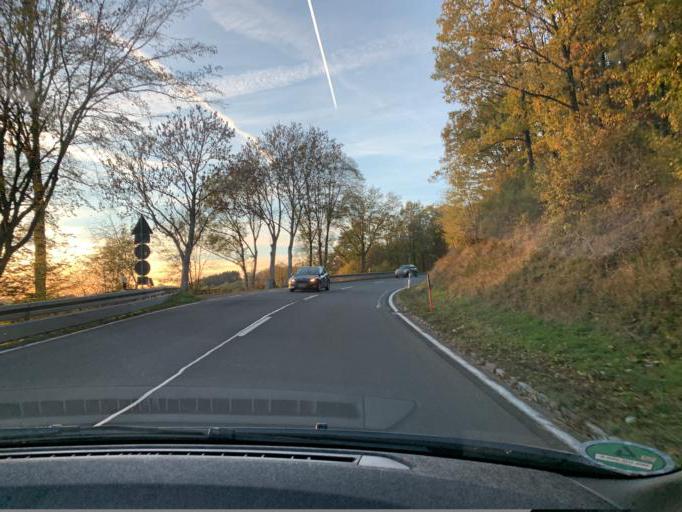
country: DE
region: North Rhine-Westphalia
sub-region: Regierungsbezirk Koln
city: Simmerath
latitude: 50.5925
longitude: 6.3606
